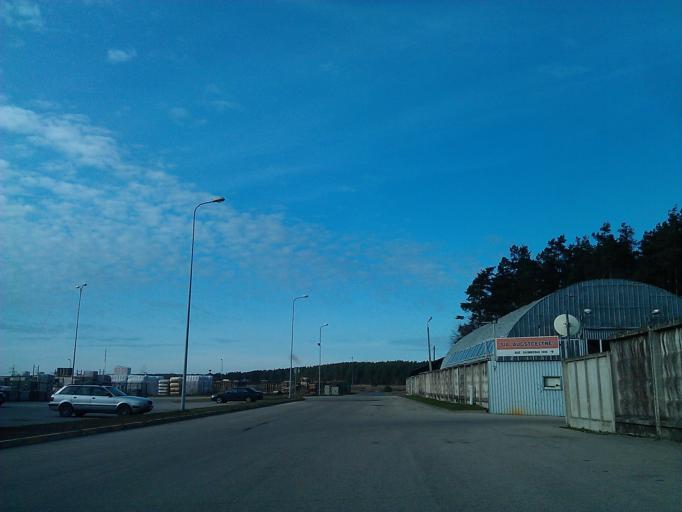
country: LV
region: Stopini
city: Ulbroka
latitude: 56.9444
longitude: 24.2597
